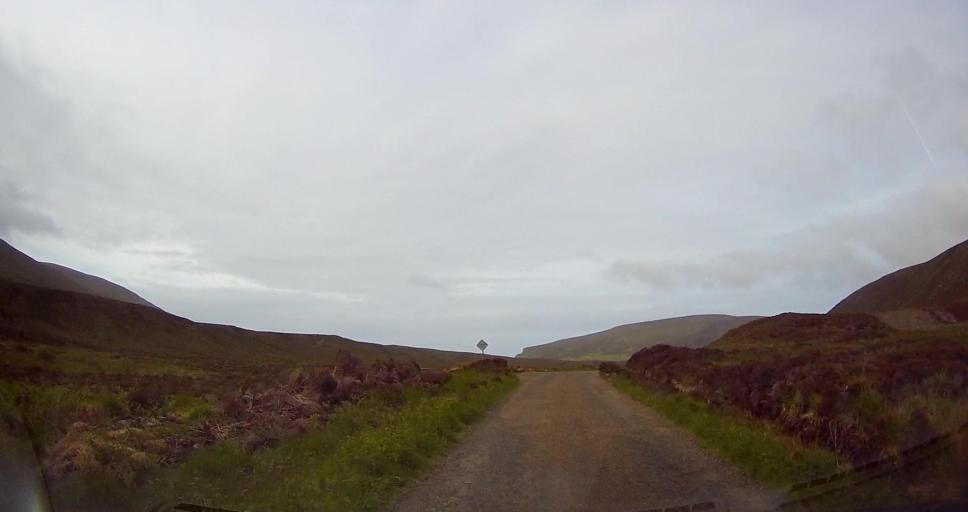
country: GB
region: Scotland
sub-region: Orkney Islands
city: Stromness
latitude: 58.8818
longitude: -3.3455
